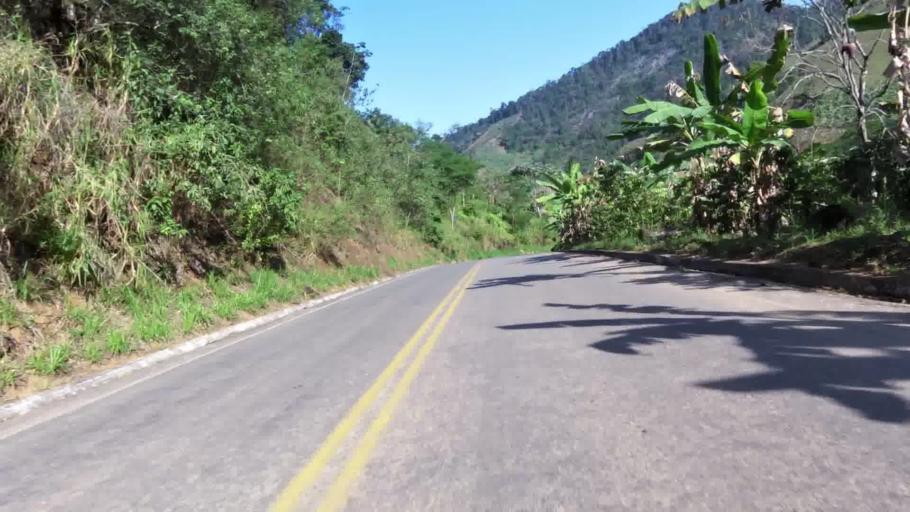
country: BR
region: Espirito Santo
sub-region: Alfredo Chaves
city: Alfredo Chaves
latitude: -20.6186
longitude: -40.7790
